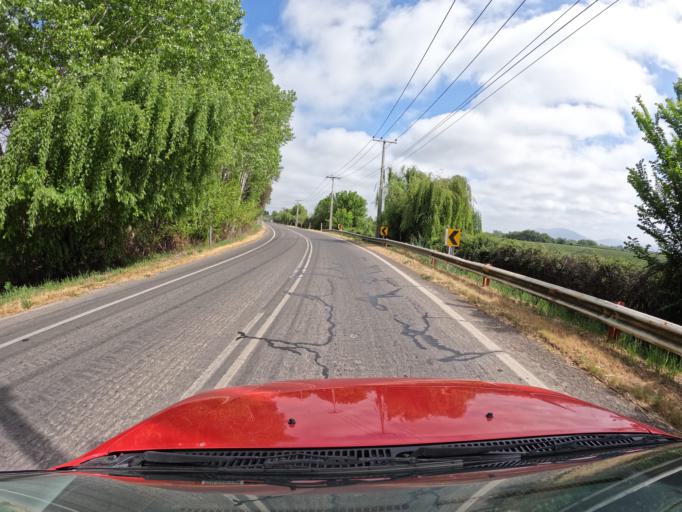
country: CL
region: O'Higgins
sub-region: Provincia de Colchagua
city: Santa Cruz
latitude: -34.6992
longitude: -71.3091
